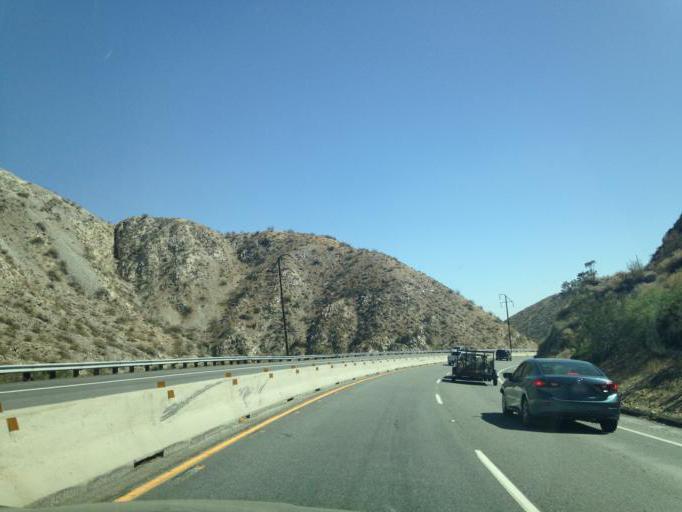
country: US
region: California
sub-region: San Bernardino County
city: Morongo Valley
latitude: 34.0192
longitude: -116.5822
